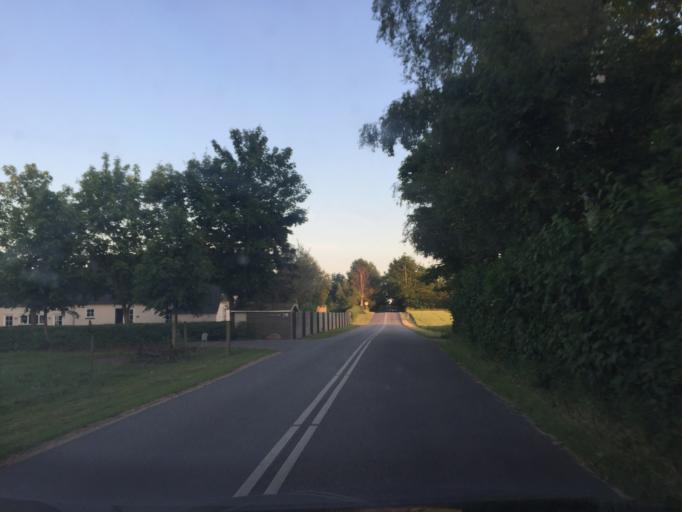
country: DK
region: Capital Region
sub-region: Egedal Kommune
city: Smorumnedre
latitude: 55.7155
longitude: 12.2658
